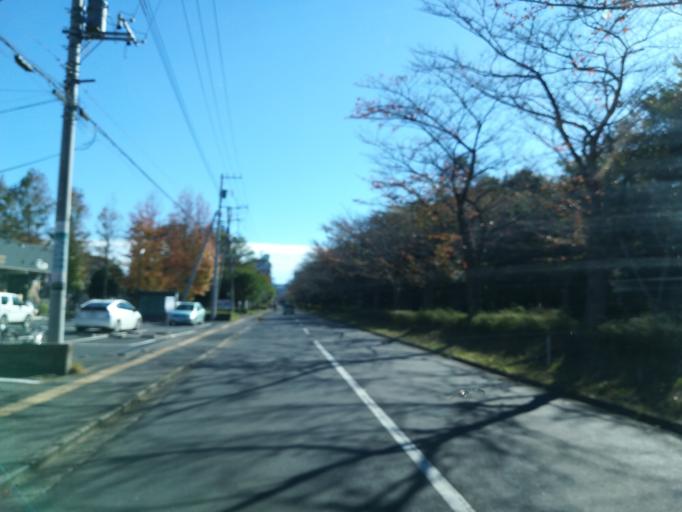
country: JP
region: Ibaraki
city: Naka
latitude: 36.0980
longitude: 140.1059
